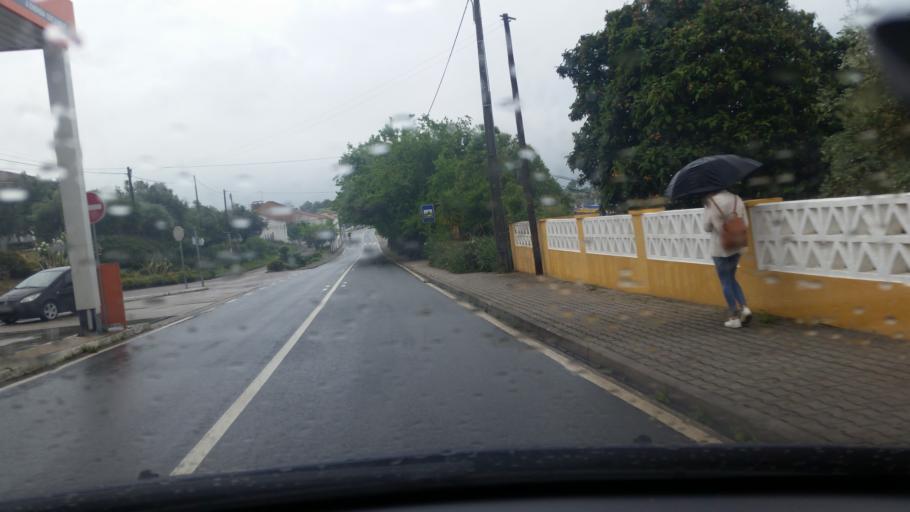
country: PT
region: Portalegre
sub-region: Ponte de Sor
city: Ponte de Sor
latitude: 39.1568
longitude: -7.9971
